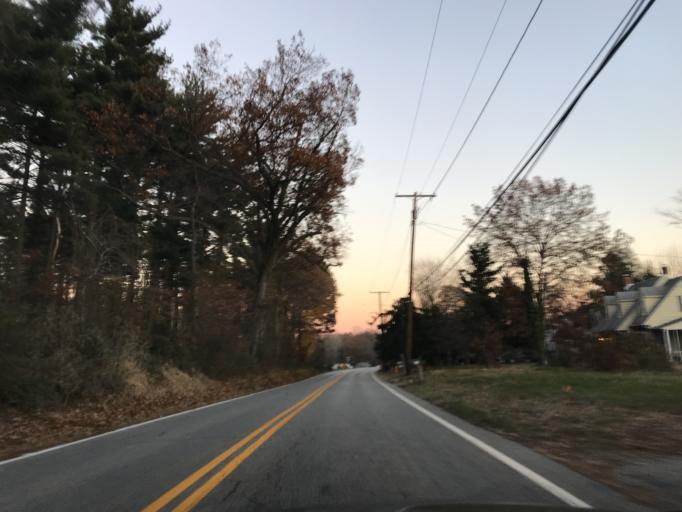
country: US
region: Maryland
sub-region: Howard County
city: West Elkridge
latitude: 39.2122
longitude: -76.7422
